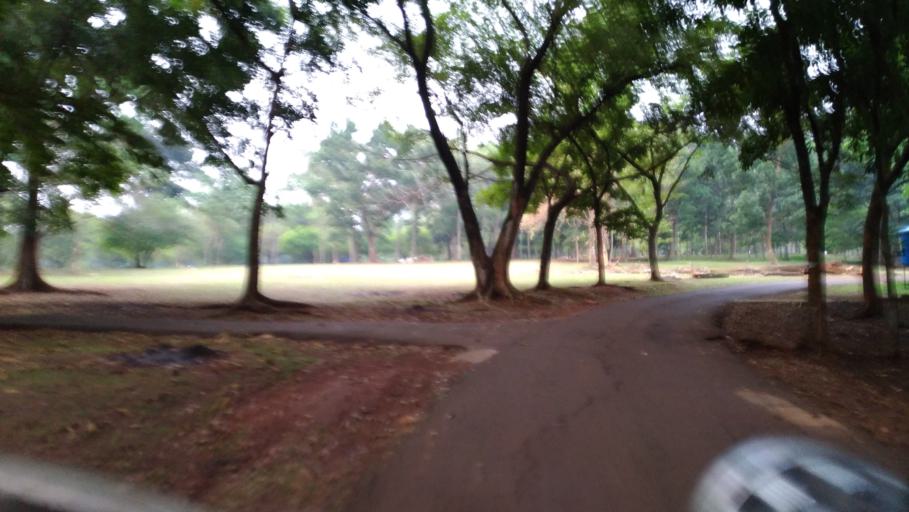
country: ID
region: West Java
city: Cileungsir
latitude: -6.3599
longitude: 106.9008
